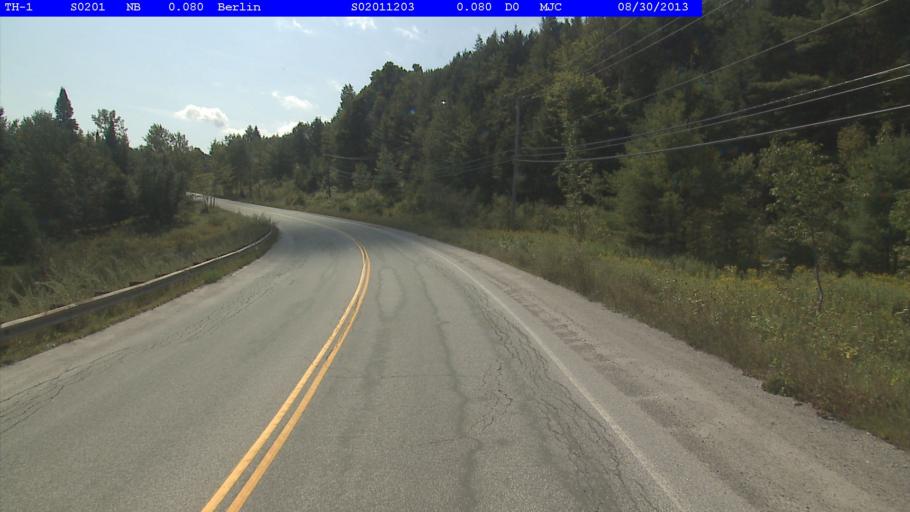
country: US
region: Vermont
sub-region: Washington County
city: Montpelier
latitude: 44.2365
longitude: -72.5651
